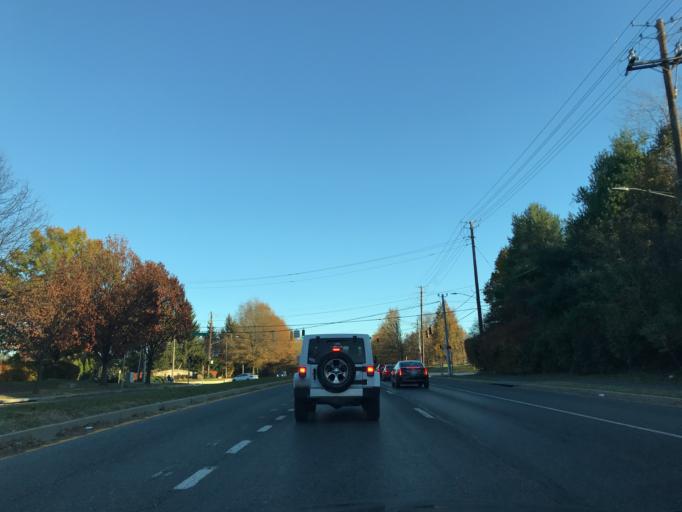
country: US
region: Maryland
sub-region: Montgomery County
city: Olney
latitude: 39.1469
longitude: -77.0515
